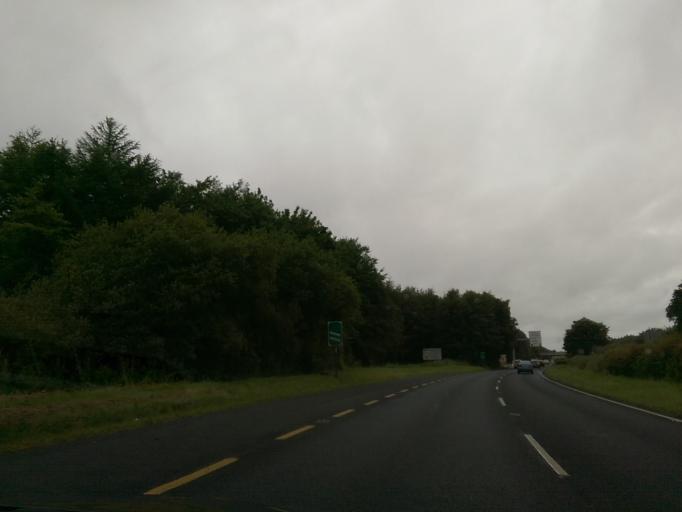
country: IE
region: Munster
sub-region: An Clar
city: Sixmilebridge
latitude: 52.6887
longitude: -8.7420
